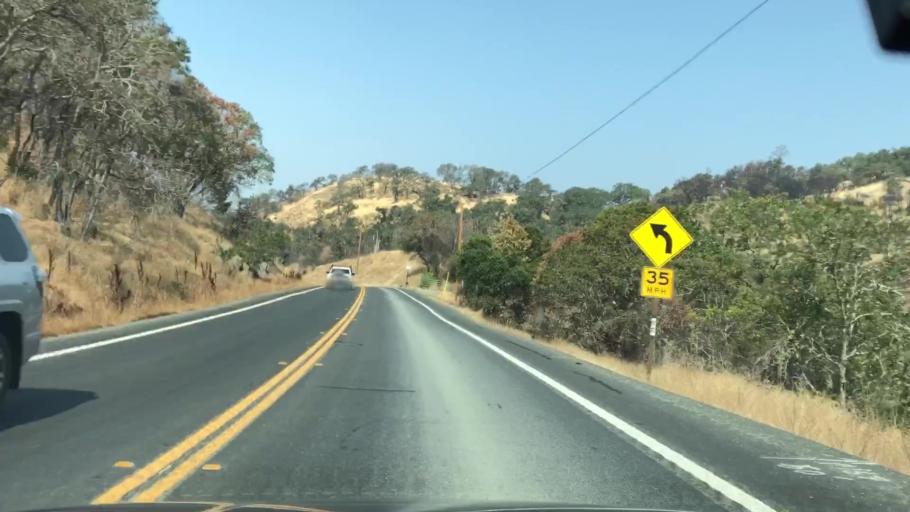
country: US
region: California
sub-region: Sonoma County
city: Larkfield-Wikiup
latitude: 38.5583
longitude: -122.6891
